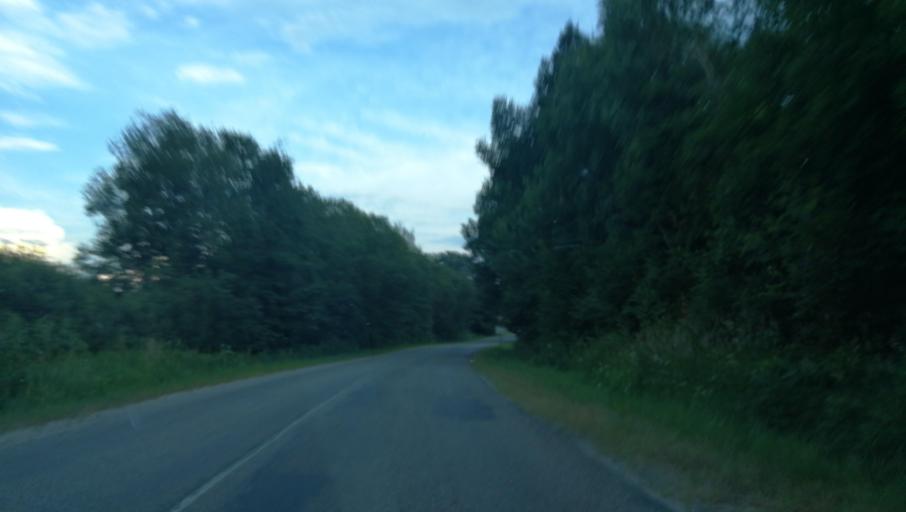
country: LV
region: Priekuli
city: Priekuli
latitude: 57.2575
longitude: 25.3688
